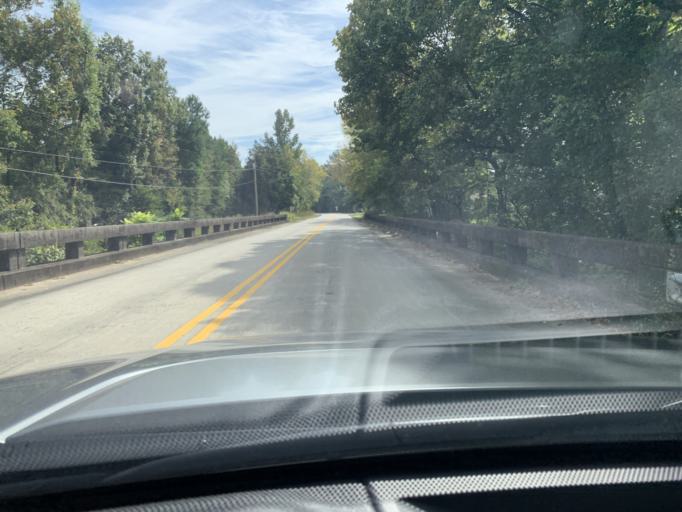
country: US
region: Georgia
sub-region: Polk County
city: Cedartown
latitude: 33.9724
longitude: -85.2702
